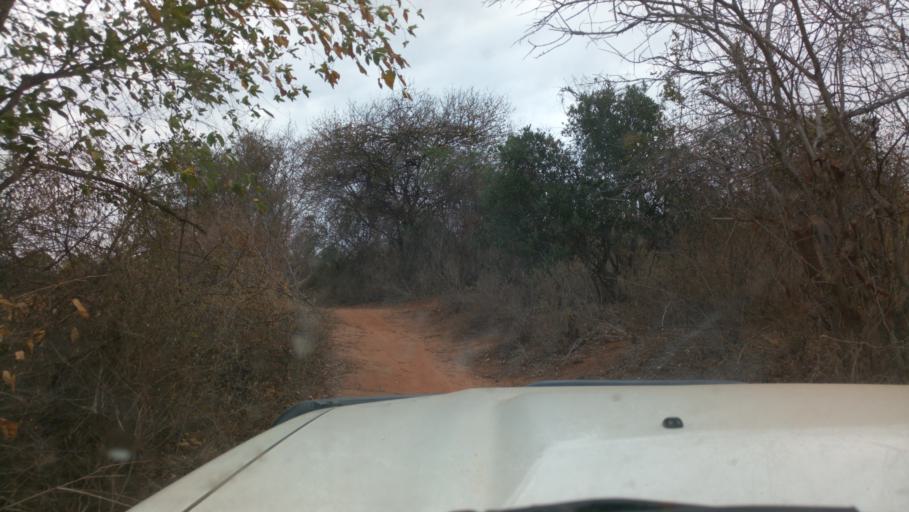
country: KE
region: Kitui
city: Kitui
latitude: -1.8412
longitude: 38.3888
